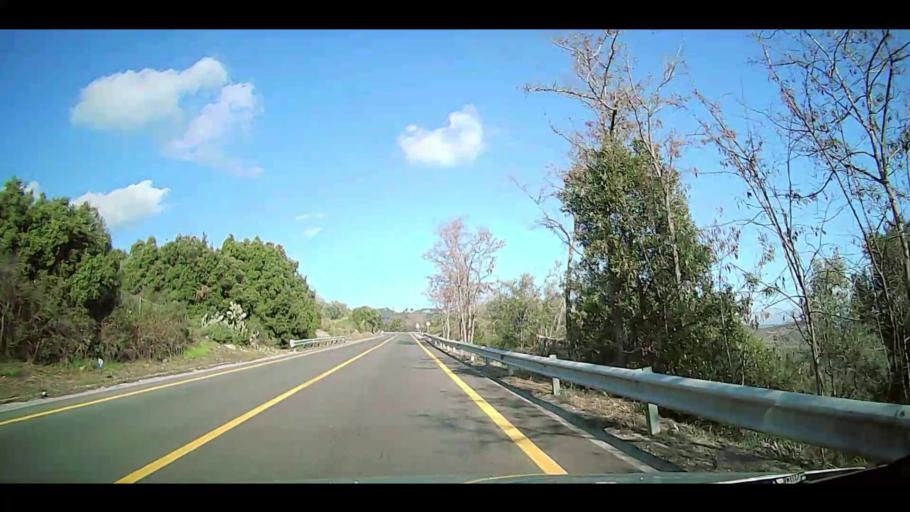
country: IT
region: Calabria
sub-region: Provincia di Crotone
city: Caccuri
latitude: 39.2290
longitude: 16.7948
